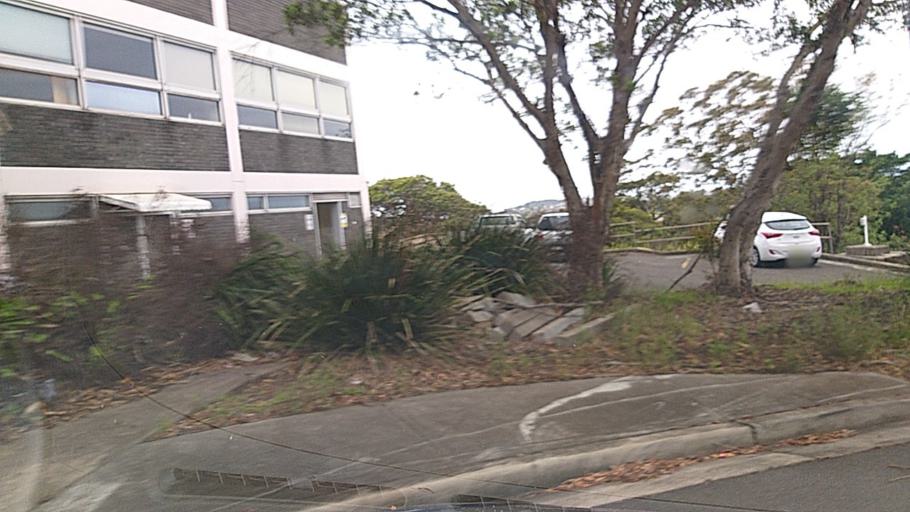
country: AU
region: New South Wales
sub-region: Wollongong
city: Lake Heights
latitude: -34.4864
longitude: 150.8809
